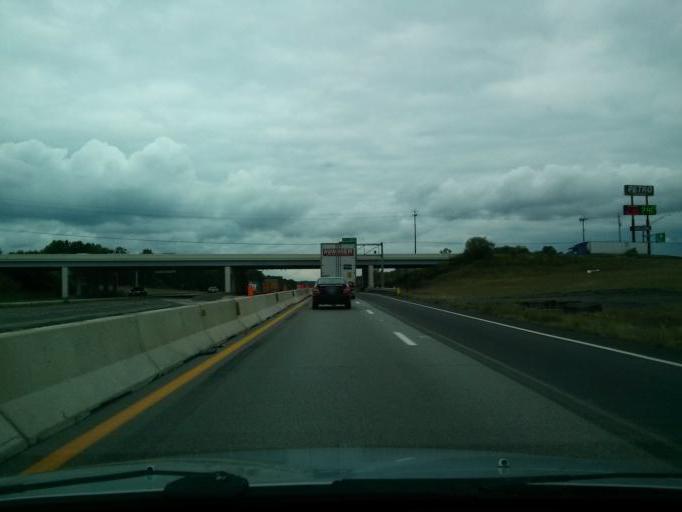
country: US
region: Ohio
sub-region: Trumbull County
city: McDonald
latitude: 41.1411
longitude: -80.7215
